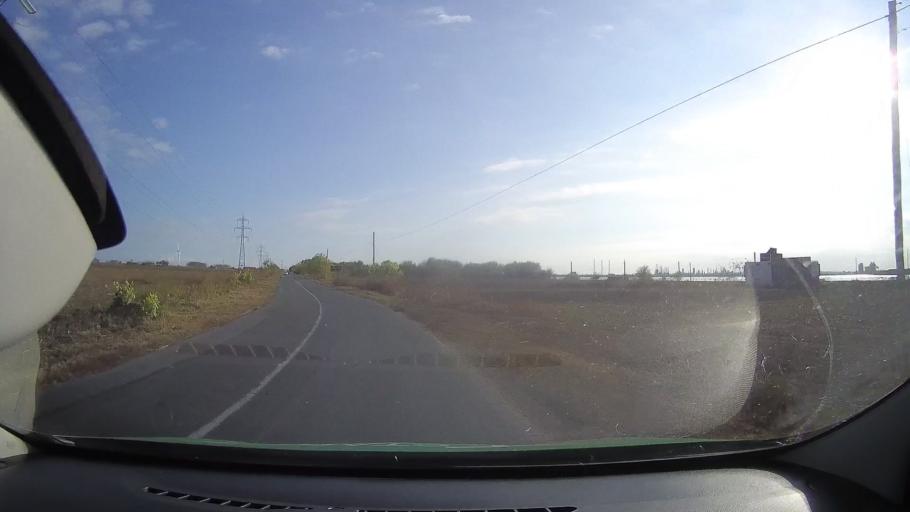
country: RO
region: Constanta
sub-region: Comuna Corbu
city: Corbu
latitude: 44.3745
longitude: 28.6640
